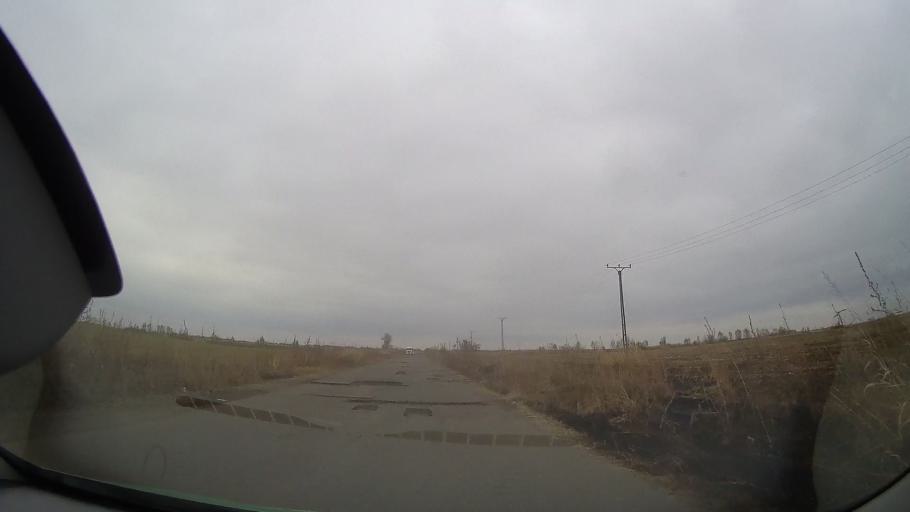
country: RO
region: Braila
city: Dudesti
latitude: 44.9285
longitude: 27.4277
